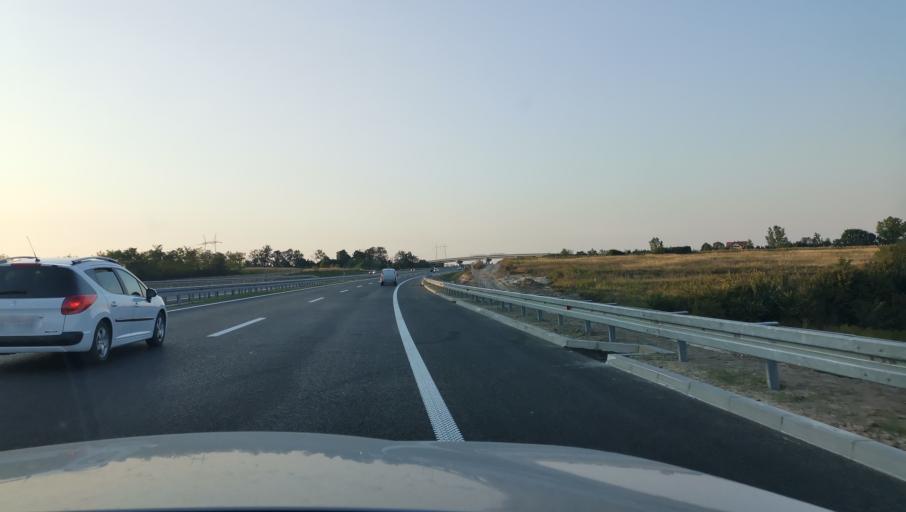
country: RS
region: Central Serbia
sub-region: Kolubarski Okrug
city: Ub
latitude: 44.3998
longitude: 20.0951
